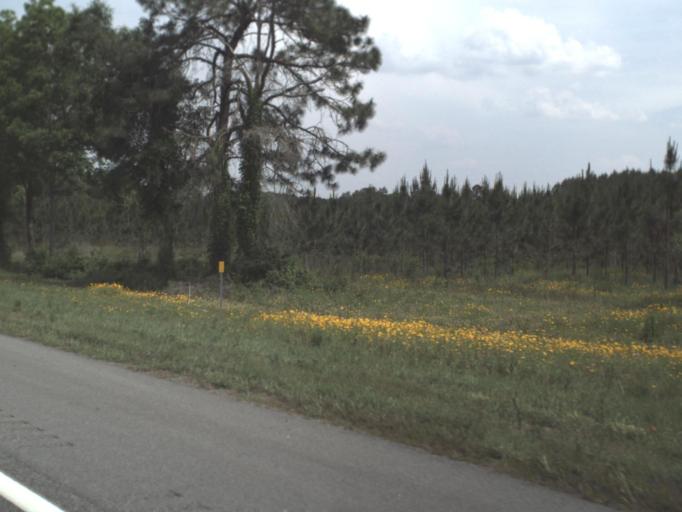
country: US
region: Florida
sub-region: Suwannee County
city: Live Oak
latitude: 30.3496
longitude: -83.0045
